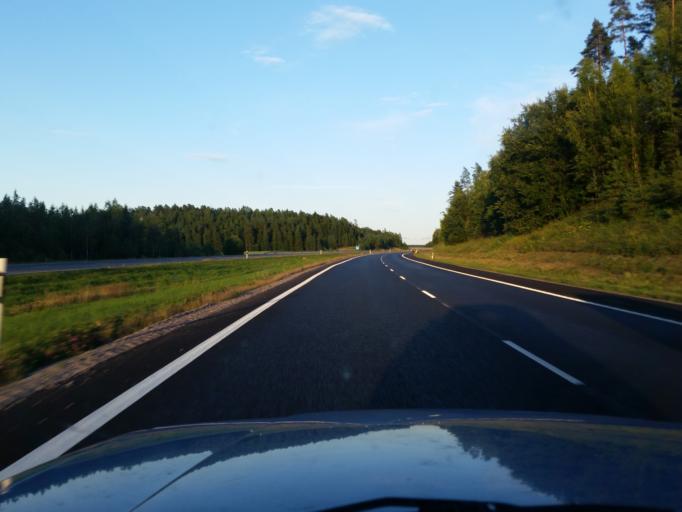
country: FI
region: Varsinais-Suomi
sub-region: Turku
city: Paimio
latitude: 60.4411
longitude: 22.6181
